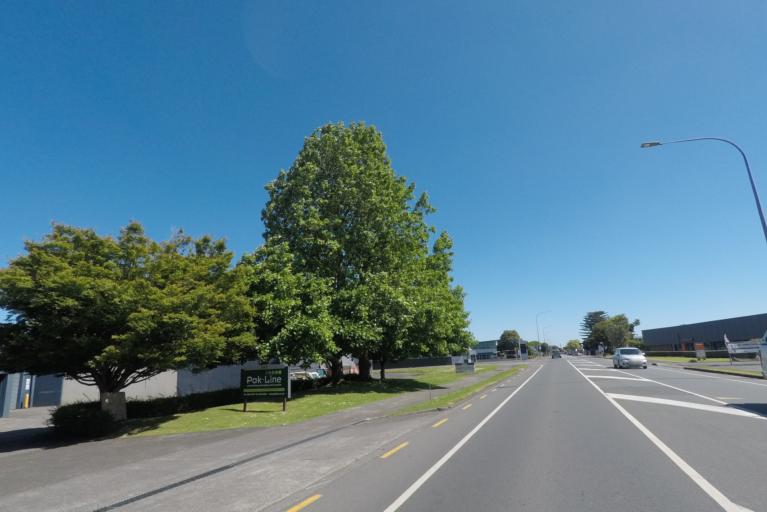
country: NZ
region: Auckland
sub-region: Auckland
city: Rosebank
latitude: -36.8767
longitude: 174.6699
